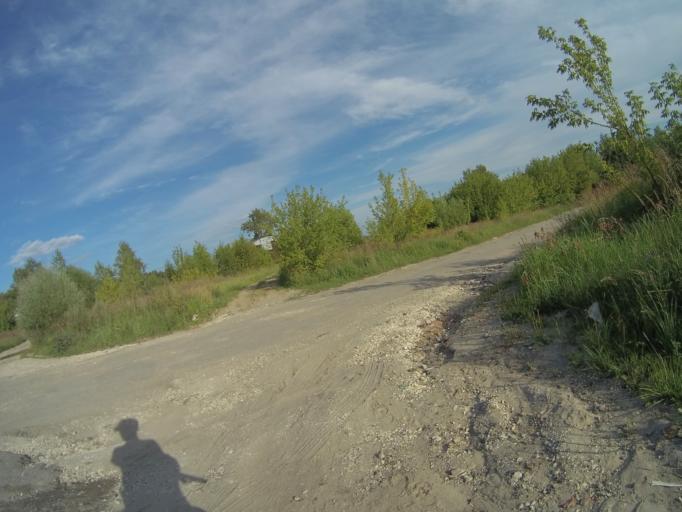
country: RU
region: Vladimir
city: Raduzhnyy
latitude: 56.0979
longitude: 40.2749
